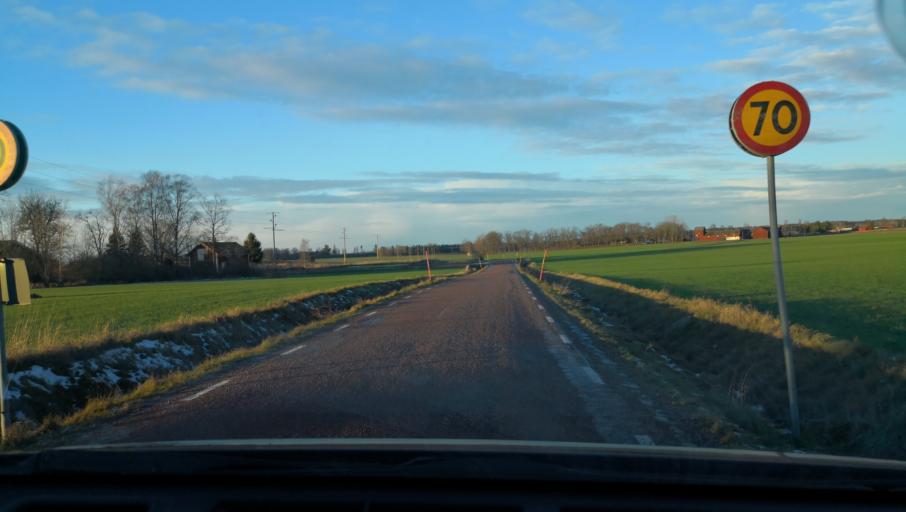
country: SE
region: Vaestmanland
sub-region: Vasteras
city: Tillberga
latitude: 59.6932
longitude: 16.6018
